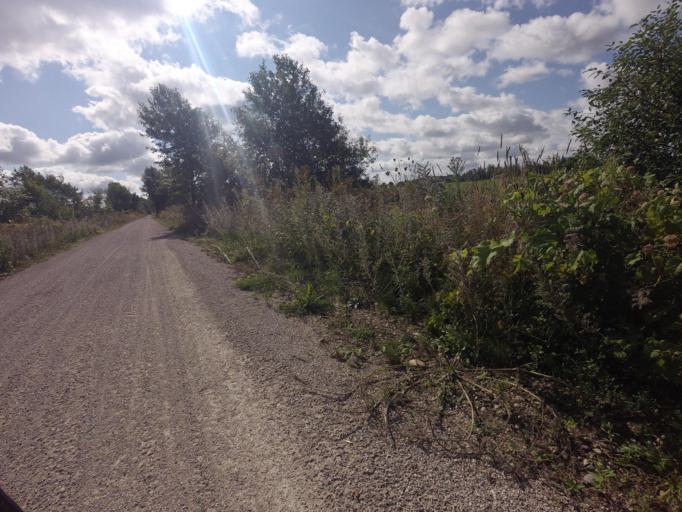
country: CA
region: Ontario
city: Huron East
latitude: 43.7217
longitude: -81.4004
